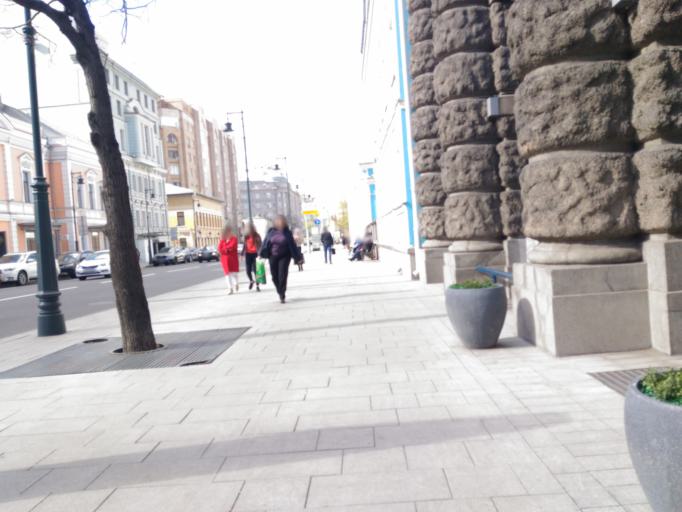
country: RU
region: Moscow
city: Moscow
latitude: 55.7683
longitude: 37.6061
